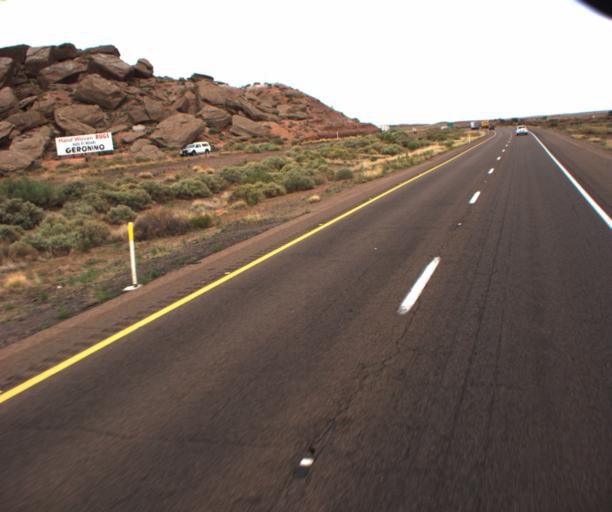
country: US
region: Arizona
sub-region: Navajo County
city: Joseph City
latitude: 34.9335
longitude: -110.2749
